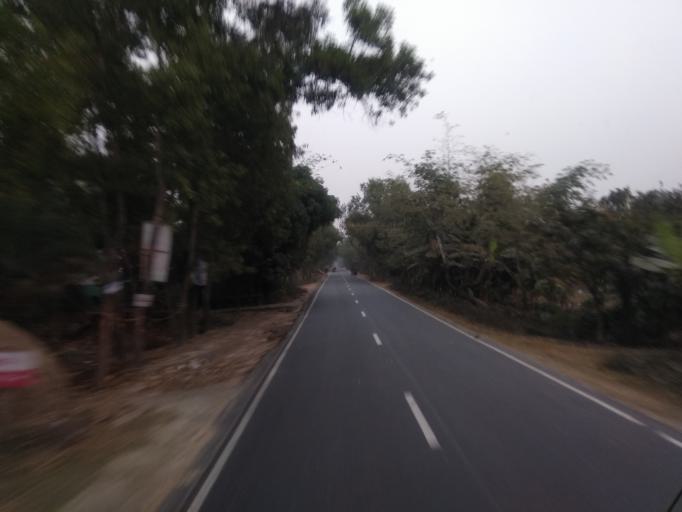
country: BD
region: Rajshahi
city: Bogra
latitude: 24.6521
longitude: 89.2595
